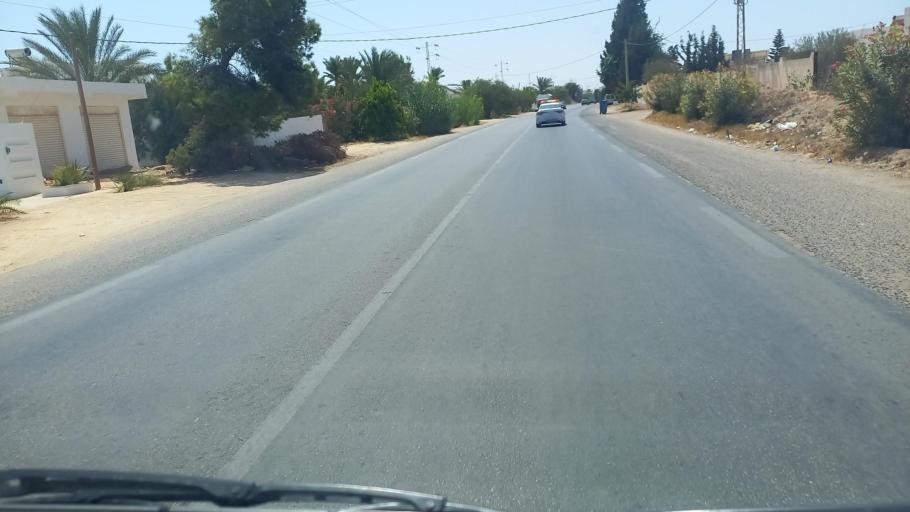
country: TN
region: Madanin
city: Houmt Souk
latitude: 33.7948
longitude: 10.8865
